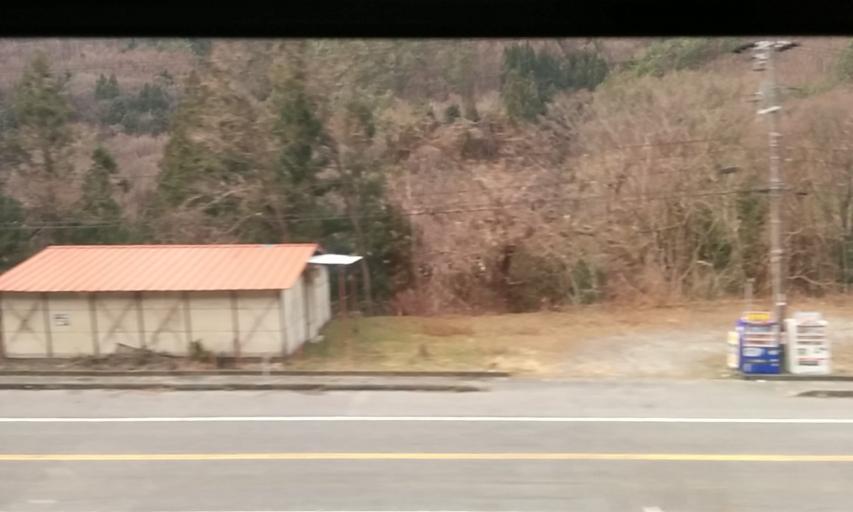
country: JP
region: Nagano
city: Shiojiri
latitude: 36.0425
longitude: 137.8893
